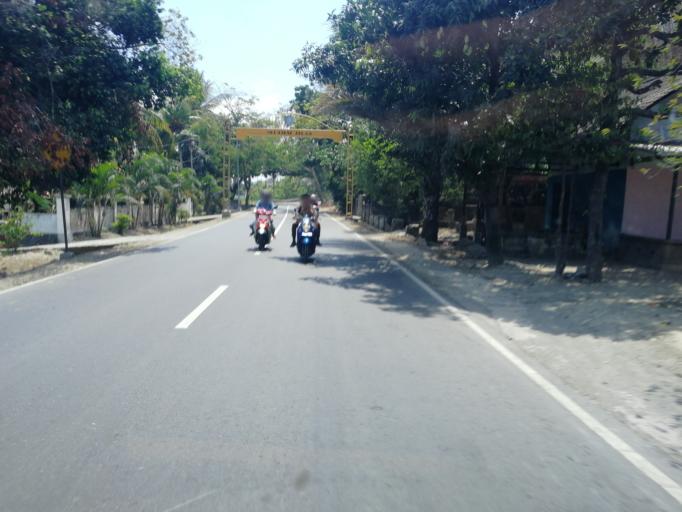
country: ID
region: West Nusa Tenggara
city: Jelateng Timur
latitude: -8.7075
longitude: 116.0806
